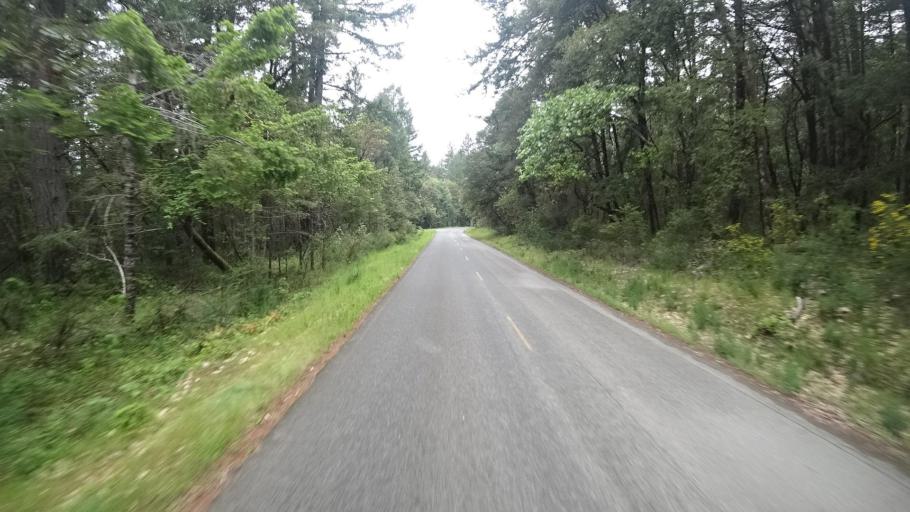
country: US
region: California
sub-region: Humboldt County
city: Willow Creek
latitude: 41.0408
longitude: -123.6584
